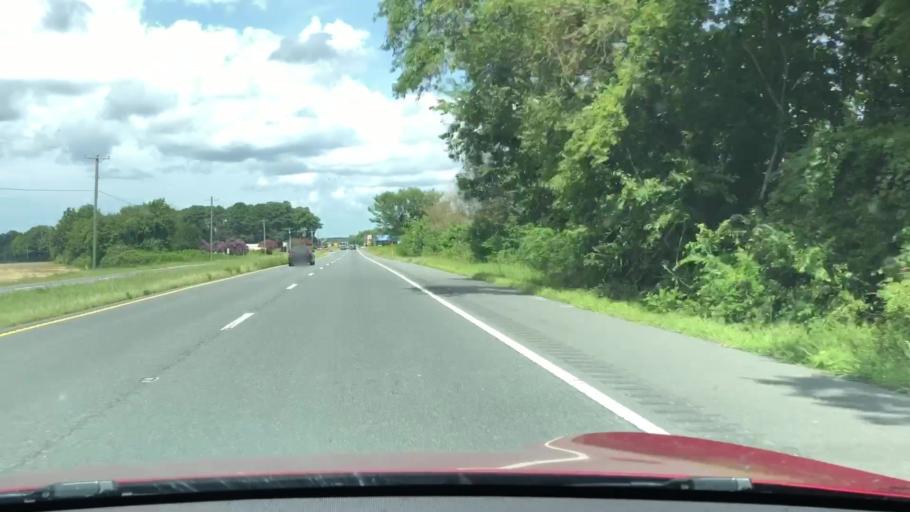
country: US
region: Virginia
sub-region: Northampton County
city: Cape Charles
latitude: 37.2609
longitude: -75.9738
